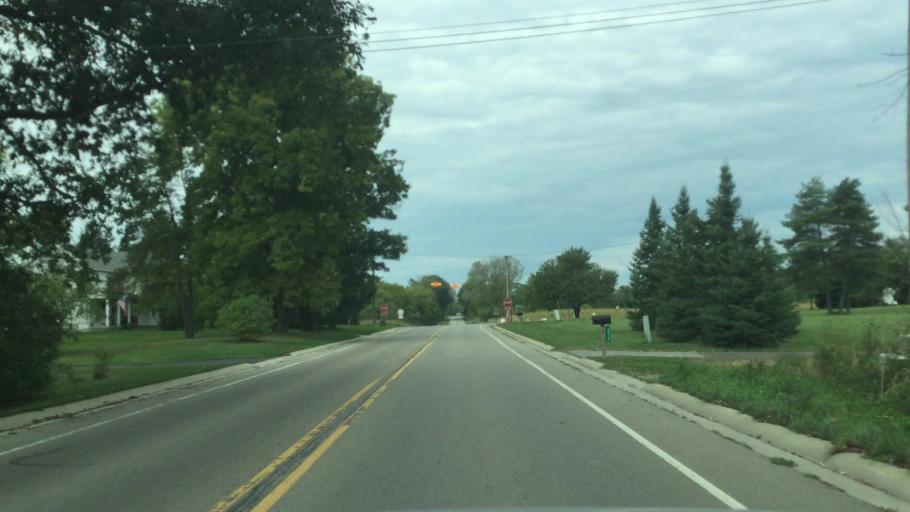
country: US
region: Michigan
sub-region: Livingston County
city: Howell
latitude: 42.6740
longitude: -83.8758
